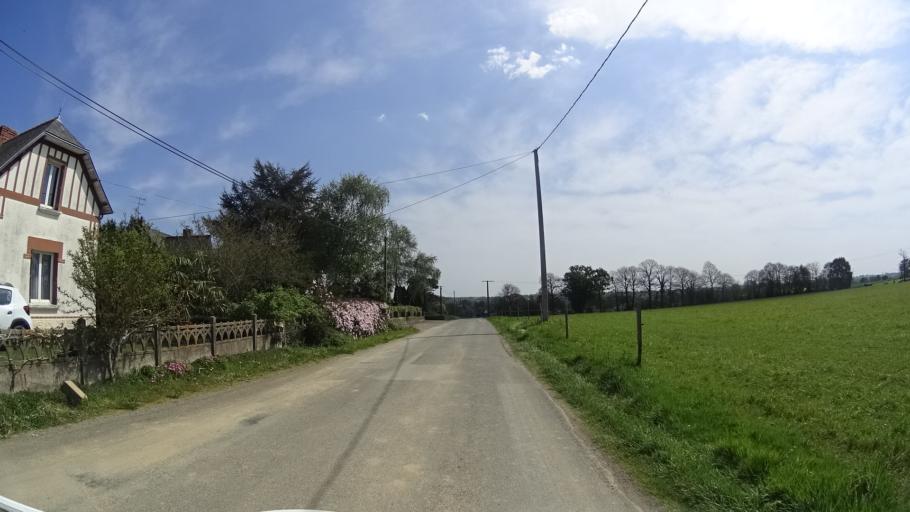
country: FR
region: Brittany
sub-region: Departement d'Ille-et-Vilaine
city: Torce
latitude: 48.0378
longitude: -1.2763
